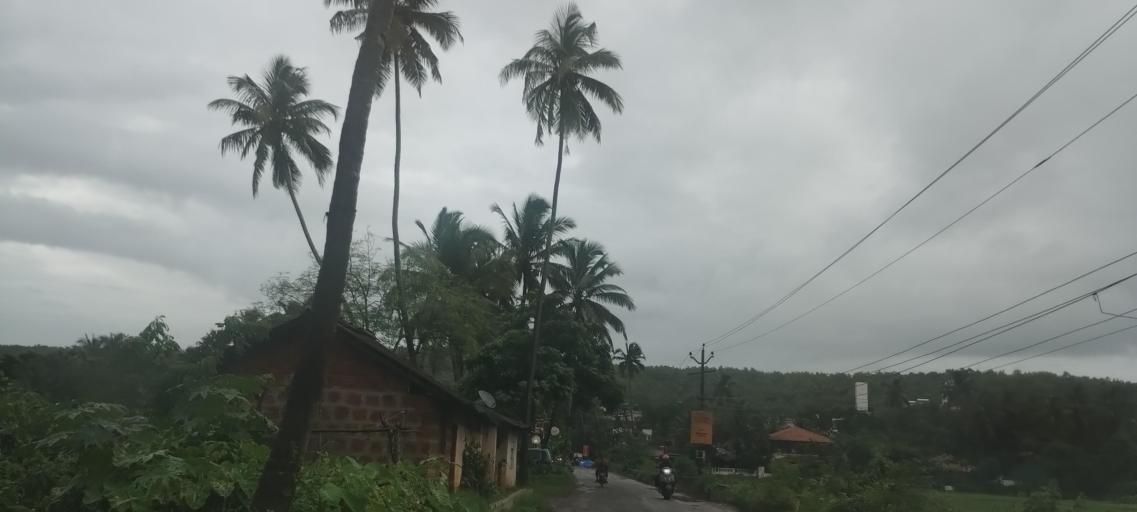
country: IN
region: Goa
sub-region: North Goa
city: Solim
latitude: 15.5959
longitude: 73.7725
